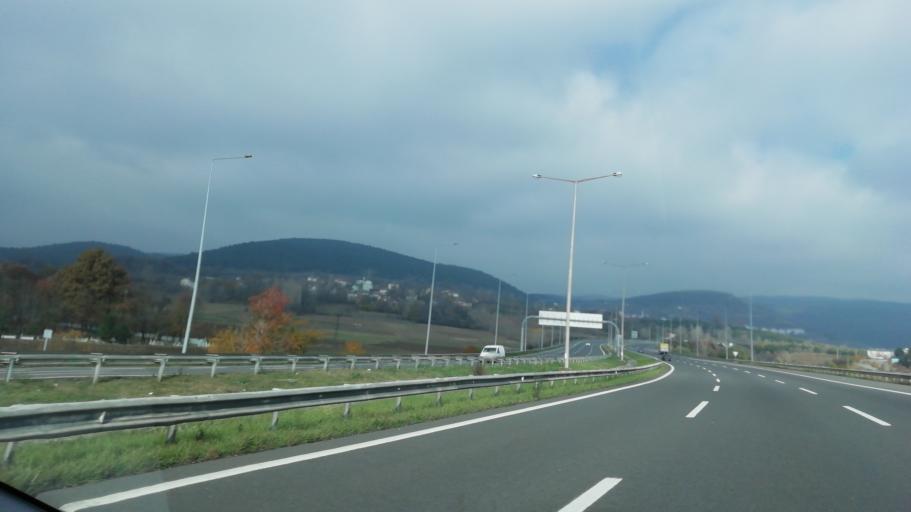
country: TR
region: Bolu
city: Bolu
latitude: 40.7434
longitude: 31.5611
